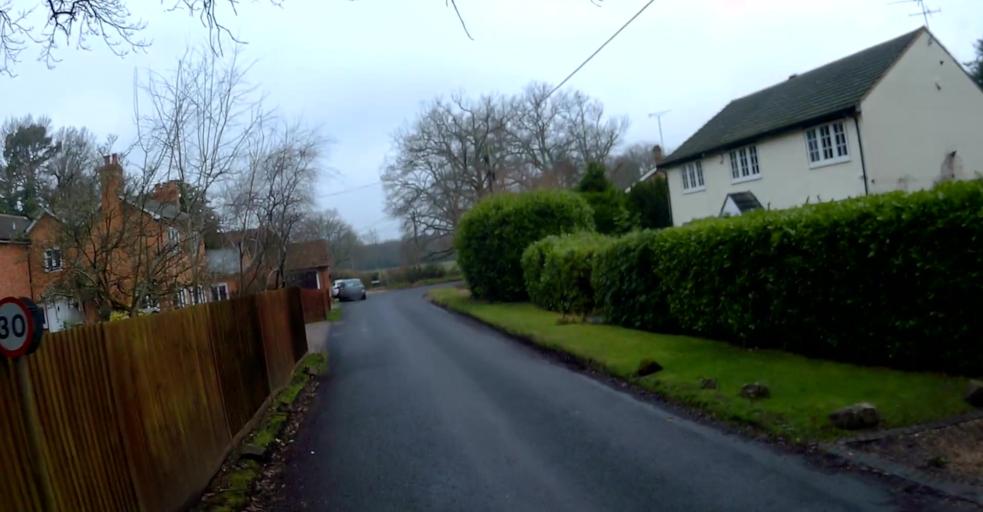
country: GB
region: England
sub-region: Hampshire
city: Eversley
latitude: 51.3549
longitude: -0.9034
